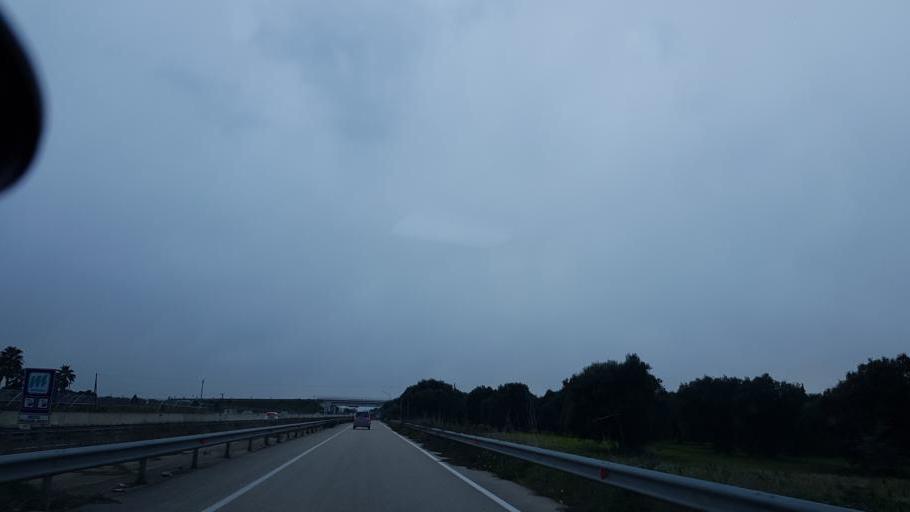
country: IT
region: Apulia
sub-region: Provincia di Brindisi
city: Mesagne
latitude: 40.5778
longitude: 17.8369
